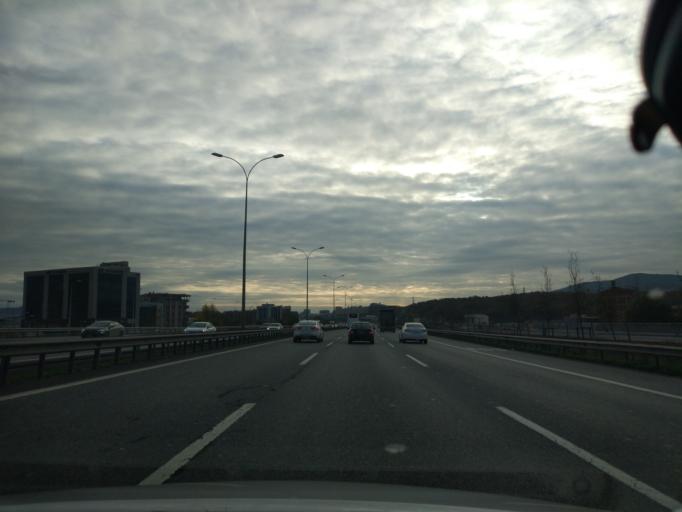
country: TR
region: Istanbul
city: Samandira
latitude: 40.9805
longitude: 29.2173
